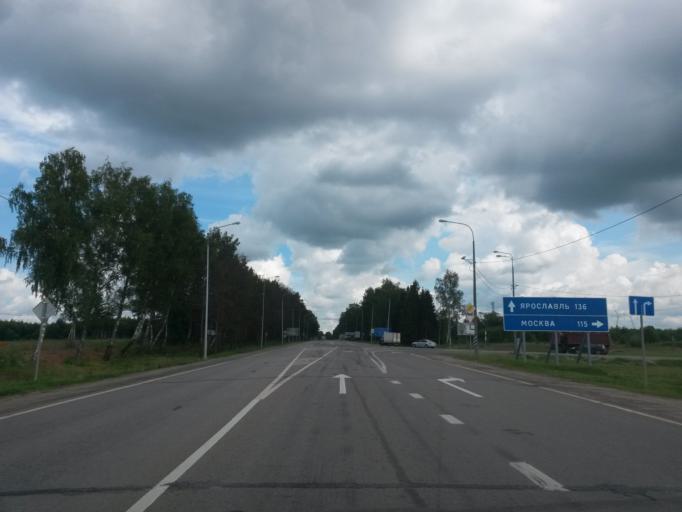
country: RU
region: Vladimir
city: Strunino
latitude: 56.5613
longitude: 38.5804
